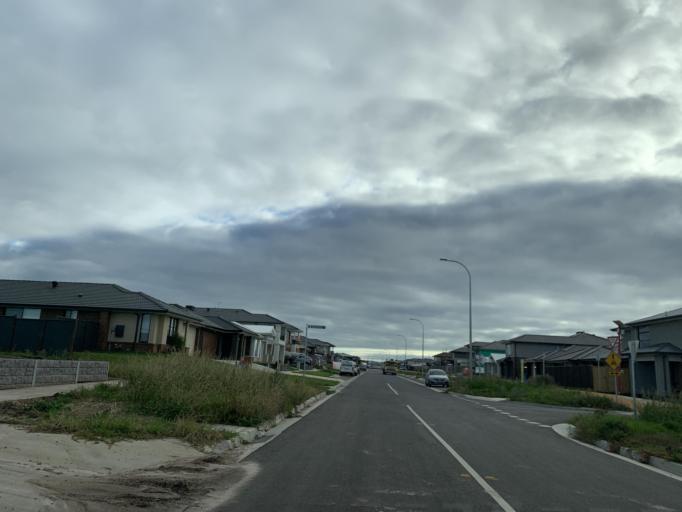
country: AU
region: Victoria
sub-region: Casey
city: Cranbourne East
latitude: -38.1273
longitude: 145.3354
